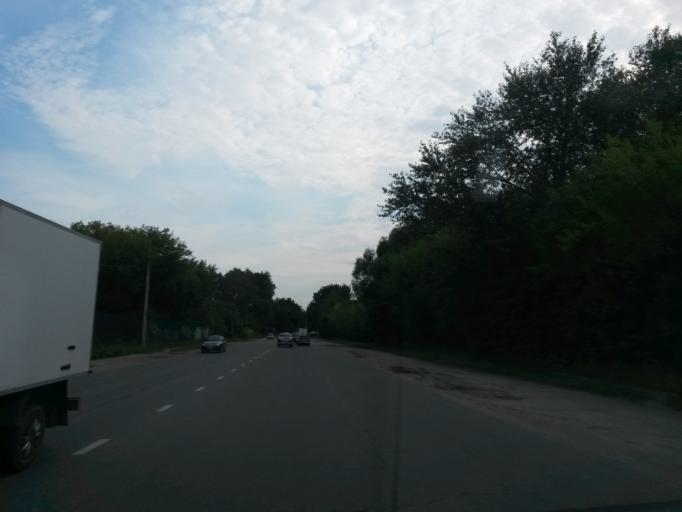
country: RU
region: Jaroslavl
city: Yaroslavl
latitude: 57.6133
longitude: 39.8400
